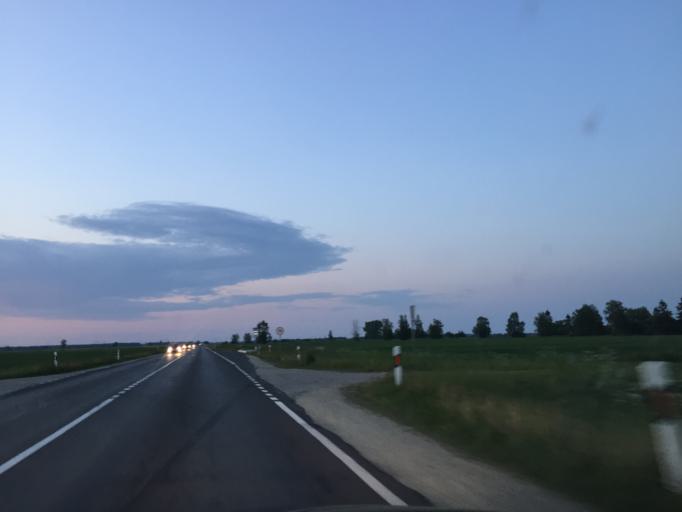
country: LT
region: Siauliu apskritis
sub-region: Joniskis
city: Joniskis
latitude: 56.0882
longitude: 23.4678
